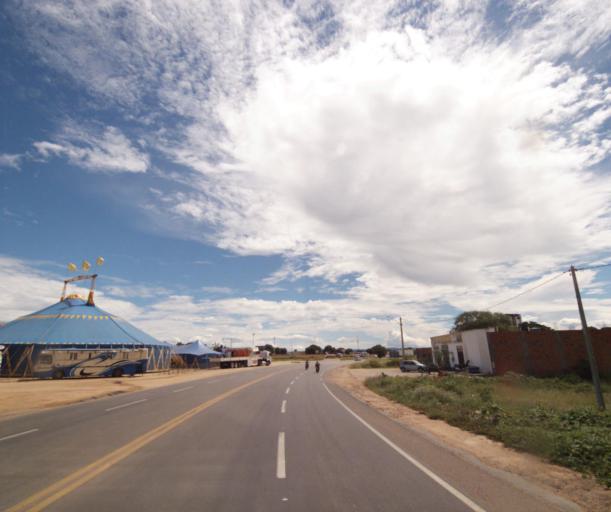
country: BR
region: Bahia
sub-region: Guanambi
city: Guanambi
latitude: -14.2351
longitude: -42.7673
